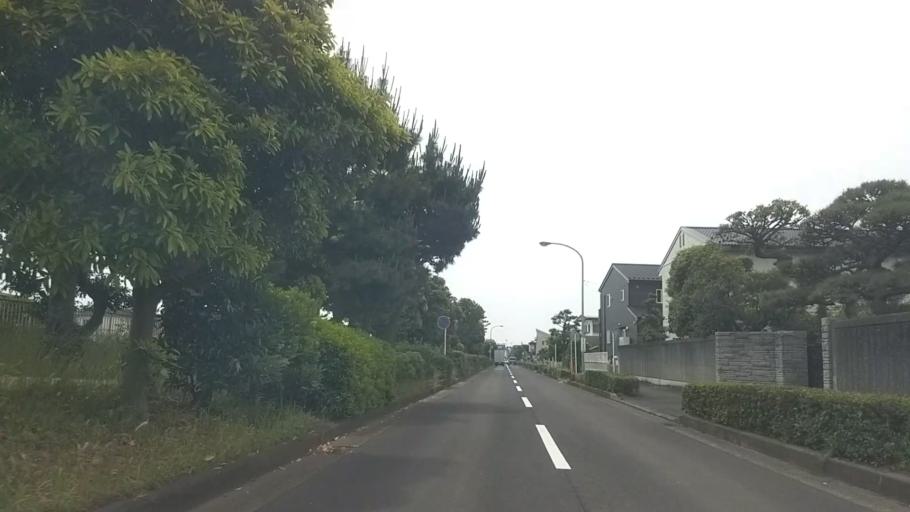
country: JP
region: Kanagawa
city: Fujisawa
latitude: 35.3251
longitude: 139.4625
